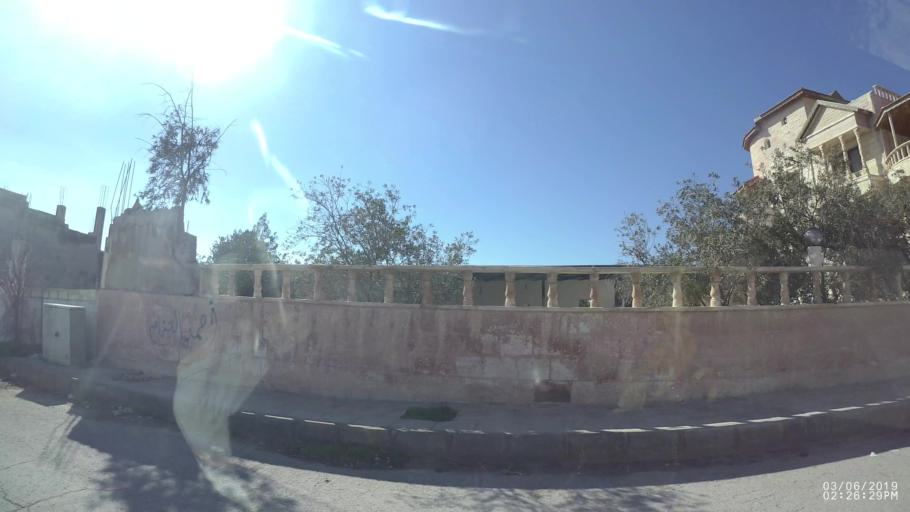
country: JO
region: Zarqa
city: Russeifa
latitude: 32.0390
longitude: 36.0329
